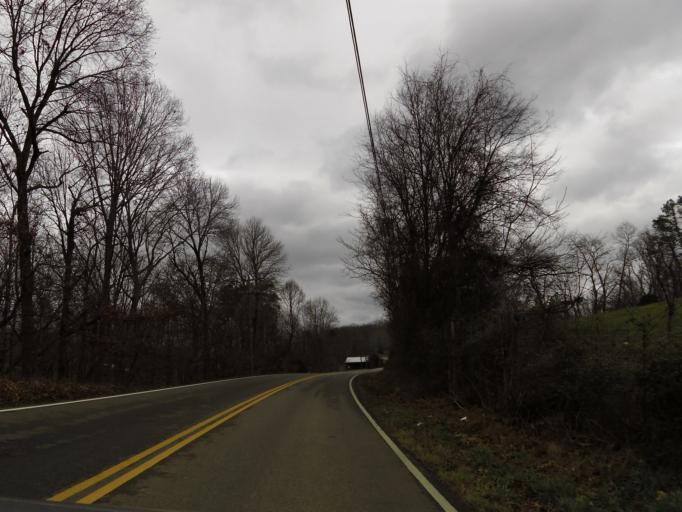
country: US
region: Tennessee
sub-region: Jefferson County
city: New Market
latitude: 36.1946
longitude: -83.5828
